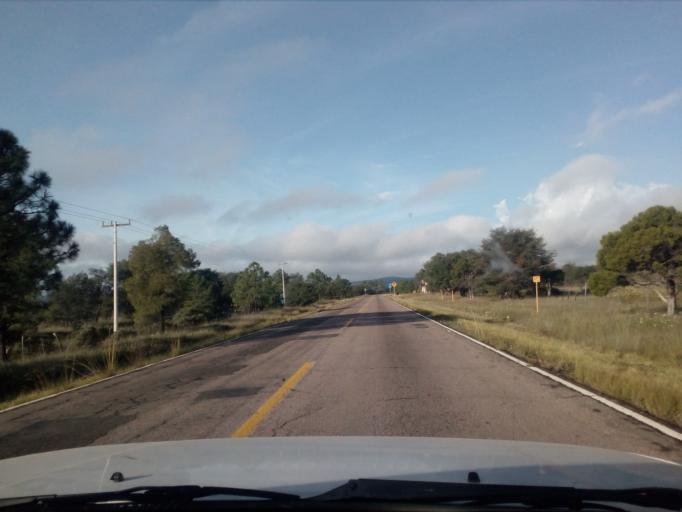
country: MX
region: Durango
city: Victoria de Durango
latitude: 23.9288
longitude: -104.9253
